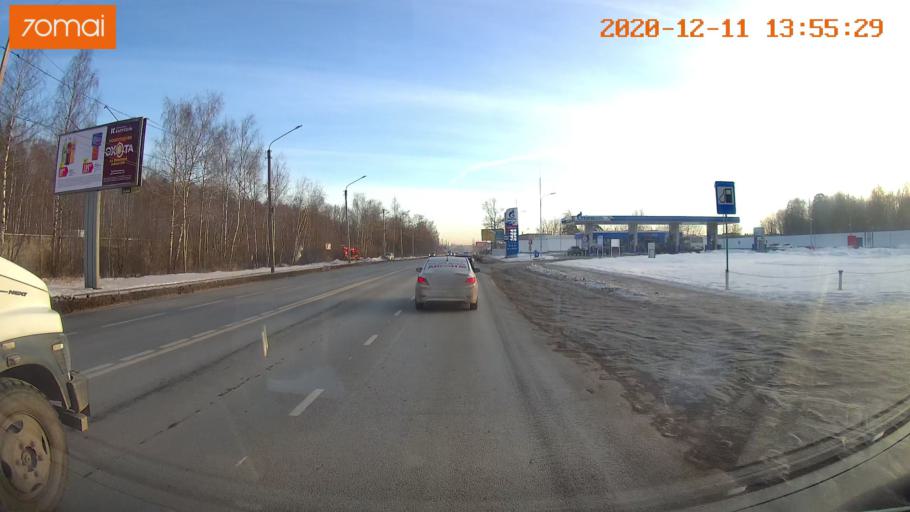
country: RU
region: Kostroma
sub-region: Kostromskoy Rayon
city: Kostroma
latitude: 57.7819
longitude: 40.9645
